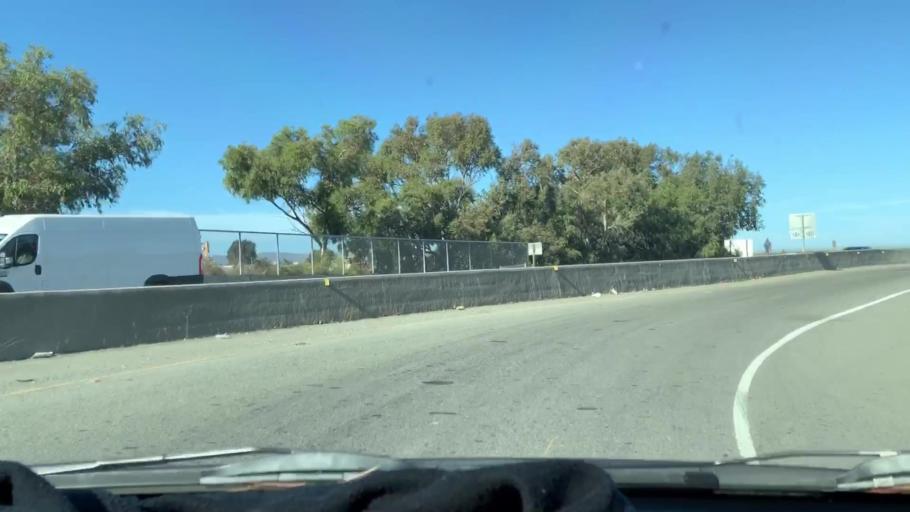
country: US
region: California
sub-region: San Mateo County
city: Millbrae
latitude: 37.6020
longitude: -122.3823
